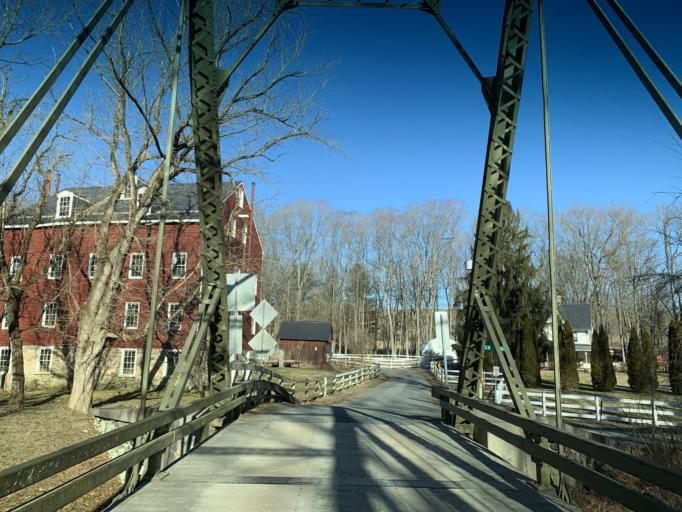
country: US
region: Maryland
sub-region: Harford County
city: South Bel Air
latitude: 39.6180
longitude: -76.2378
